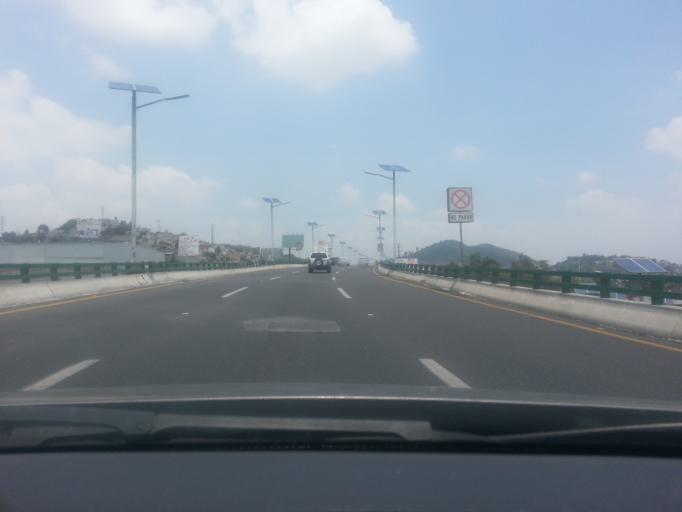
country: MX
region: Mexico
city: Tlalnepantla
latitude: 19.5763
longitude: -99.2079
